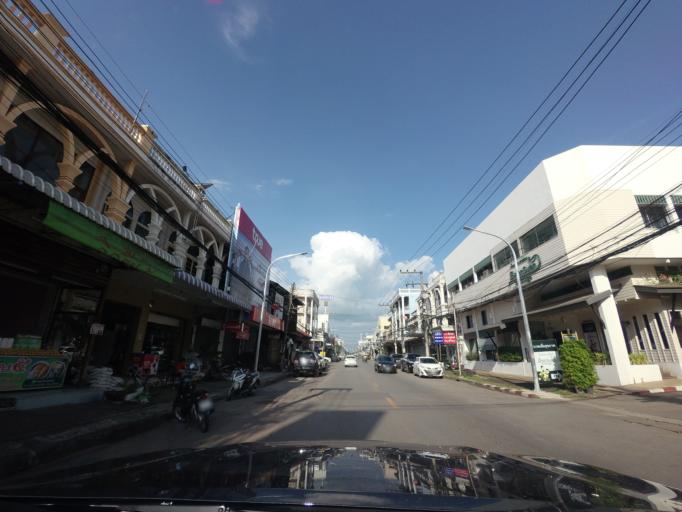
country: TH
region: Nong Khai
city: Nong Khai
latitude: 17.8830
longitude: 102.7493
